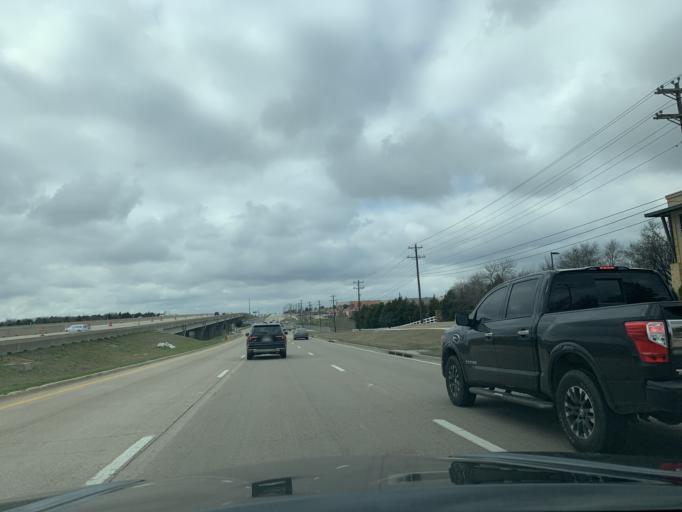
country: US
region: Texas
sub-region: Collin County
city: Allen
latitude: 33.1308
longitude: -96.7181
